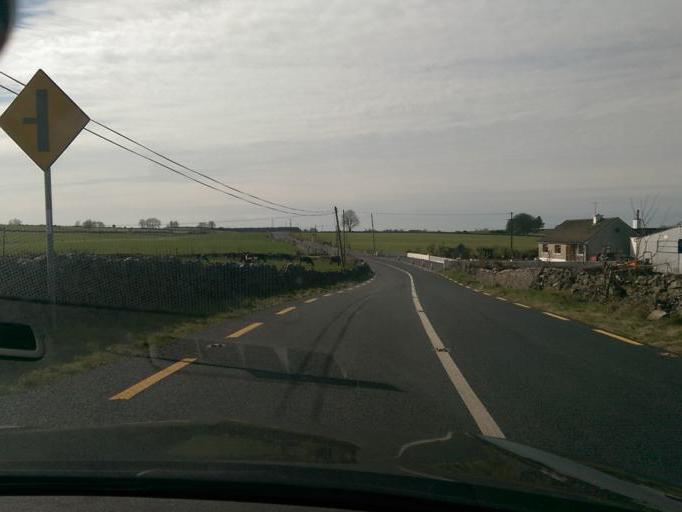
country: IE
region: Connaught
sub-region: County Galway
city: Athenry
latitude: 53.4845
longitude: -8.5885
